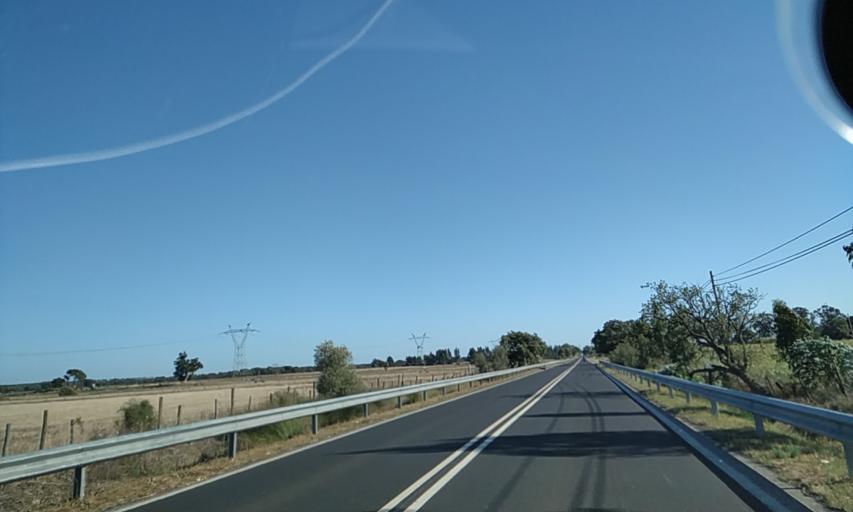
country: PT
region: Santarem
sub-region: Benavente
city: Samora Correia
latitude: 38.8707
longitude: -8.8812
